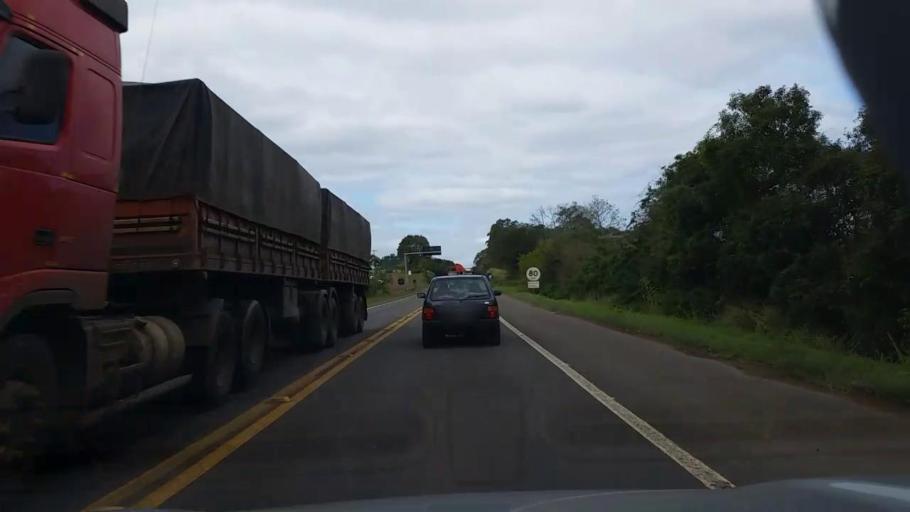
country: BR
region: Rio Grande do Sul
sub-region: Arroio Do Meio
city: Arroio do Meio
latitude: -29.4059
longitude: -52.0341
